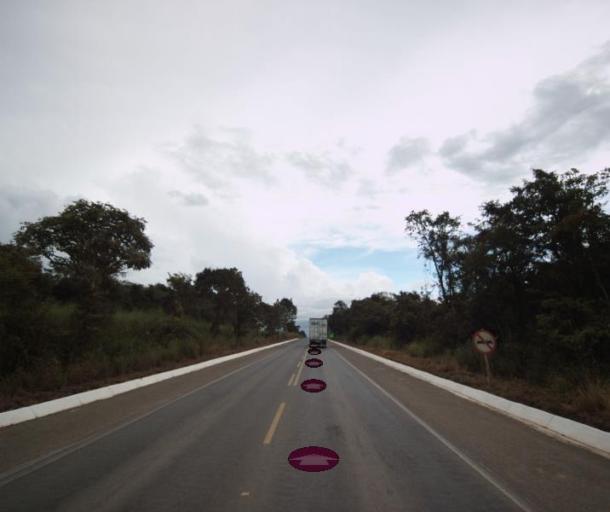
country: BR
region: Goias
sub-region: Itapaci
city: Itapaci
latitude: -14.9099
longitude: -49.3537
